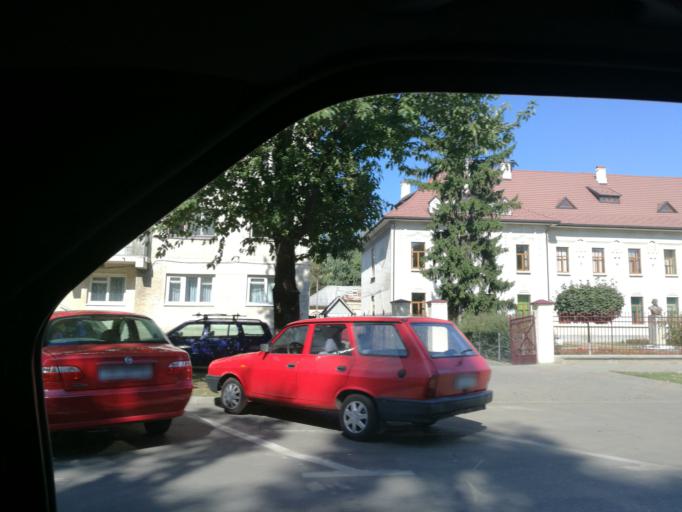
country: RO
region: Suceava
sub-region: Municipiul Suceava
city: Radauti
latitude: 47.8415
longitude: 25.9229
